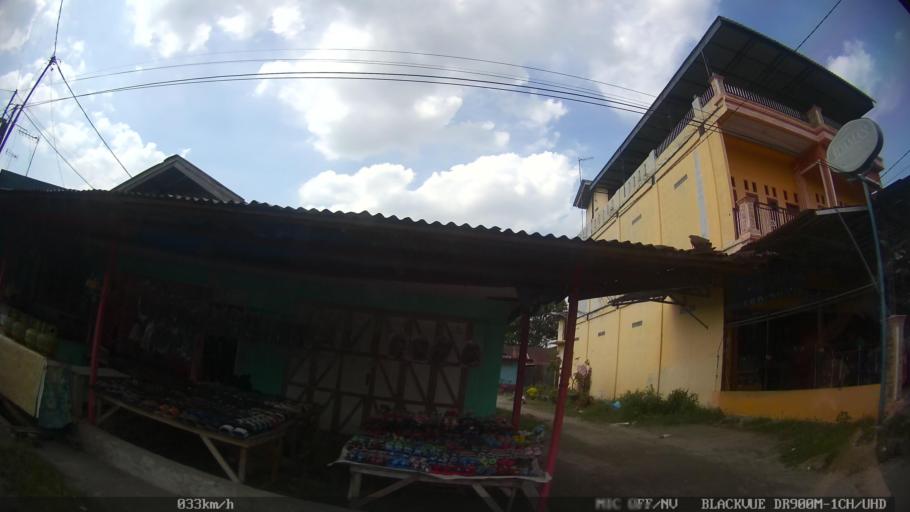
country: ID
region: North Sumatra
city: Binjai
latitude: 3.6131
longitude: 98.5018
